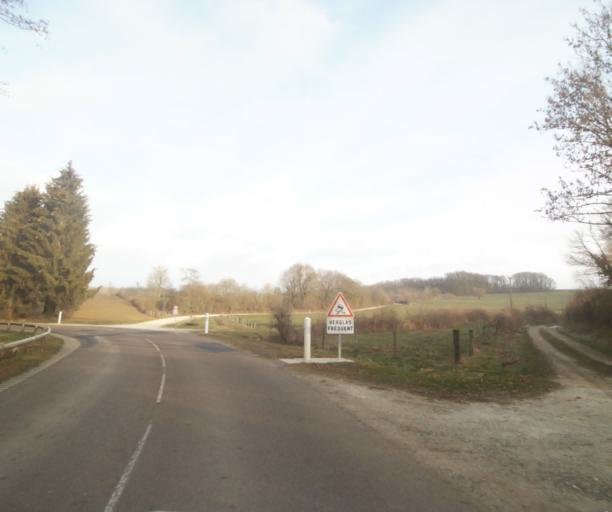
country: FR
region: Champagne-Ardenne
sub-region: Departement de la Marne
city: Sermaize-les-Bains
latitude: 48.7413
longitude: 4.9074
